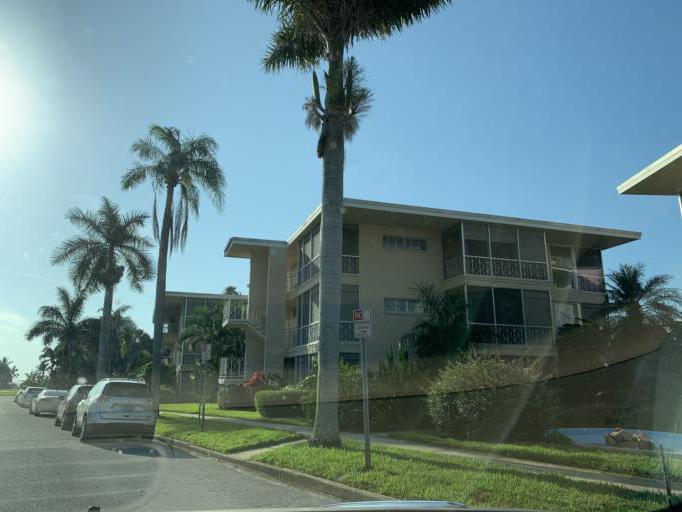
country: US
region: Florida
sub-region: Pinellas County
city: Saint Petersburg
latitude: 27.7831
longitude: -82.6274
